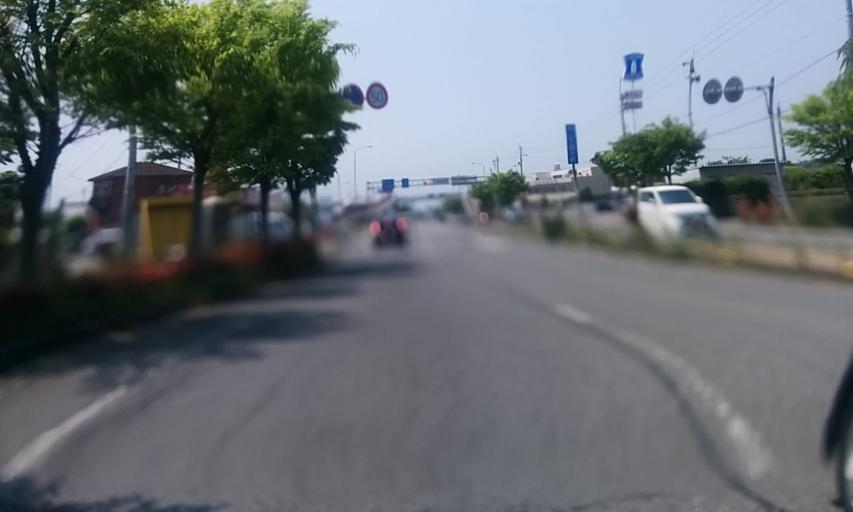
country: JP
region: Ehime
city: Saijo
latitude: 33.9197
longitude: 133.2374
